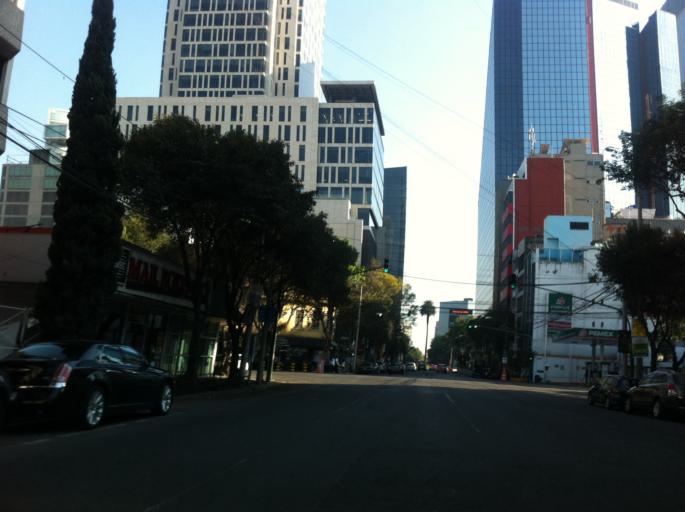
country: MX
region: Mexico City
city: Cuauhtemoc
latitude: 19.4311
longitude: -99.1649
